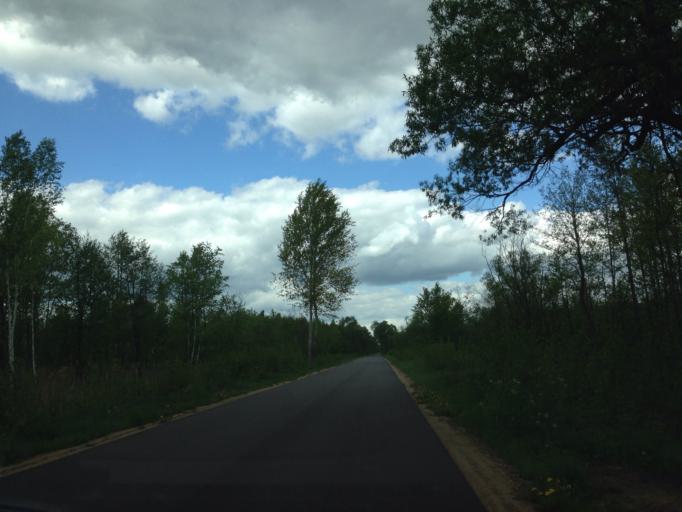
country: PL
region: Podlasie
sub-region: Powiat bialostocki
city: Tykocin
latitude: 53.3082
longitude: 22.6035
